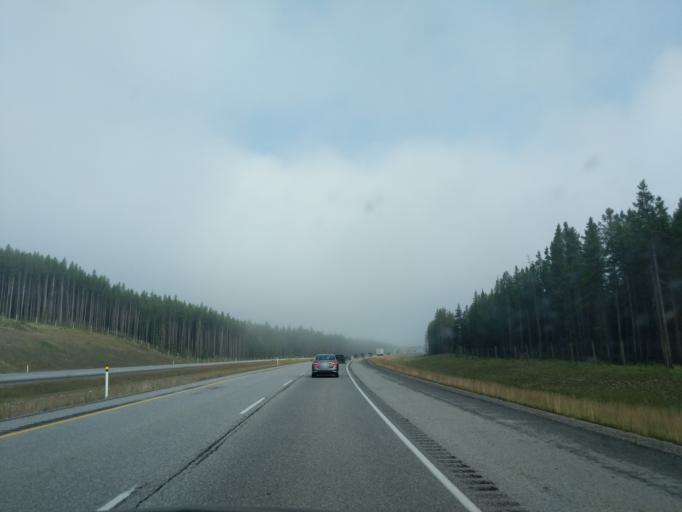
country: CA
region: Alberta
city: Lake Louise
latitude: 51.2686
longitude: -115.9464
